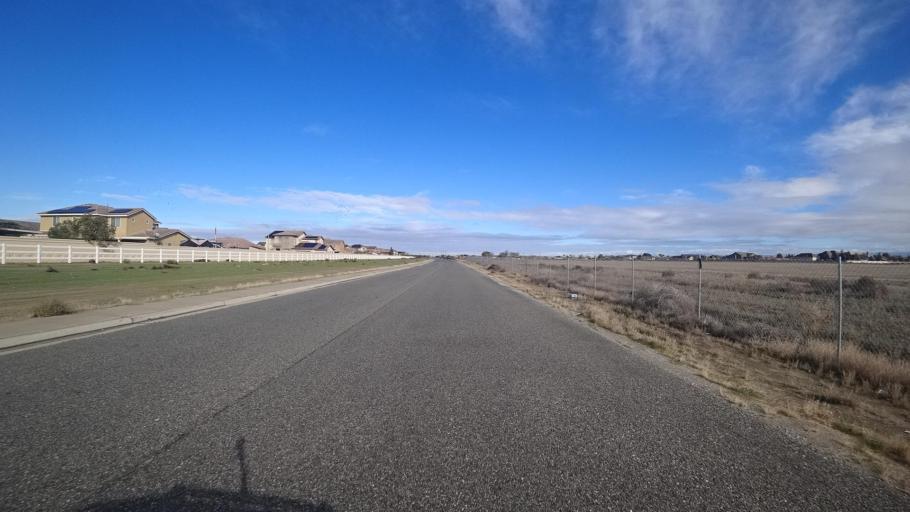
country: US
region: California
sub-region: Kern County
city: Rosedale
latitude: 35.3933
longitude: -119.1723
